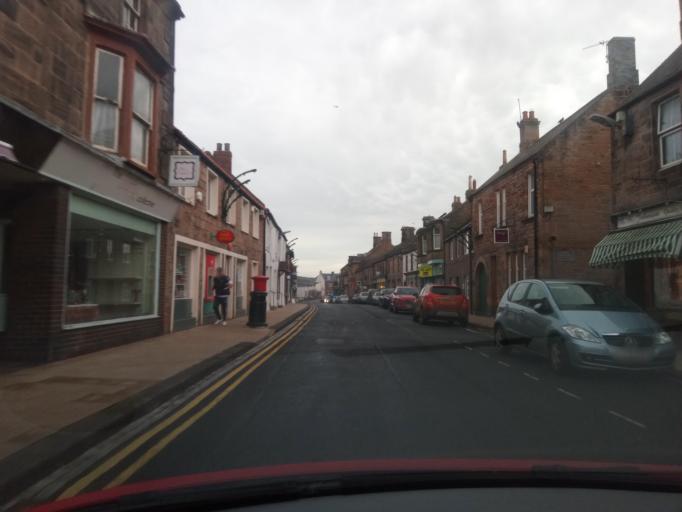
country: GB
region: England
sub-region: Northumberland
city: Wooler
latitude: 55.5470
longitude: -2.0170
